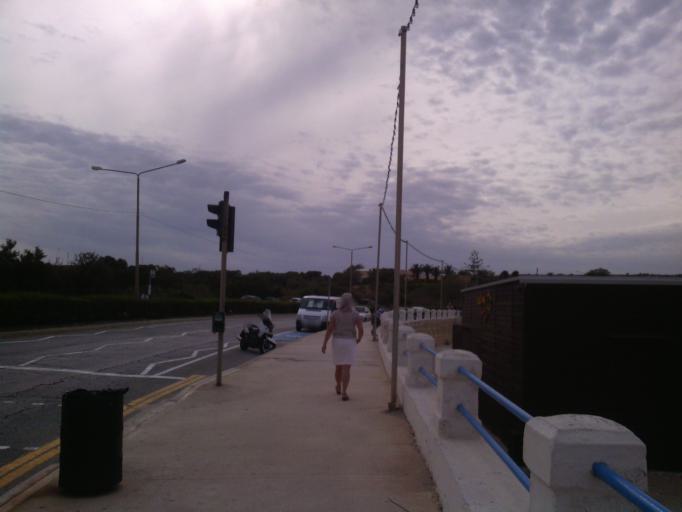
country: MT
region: Il-Mellieha
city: Mellieha
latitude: 35.9662
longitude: 14.3533
